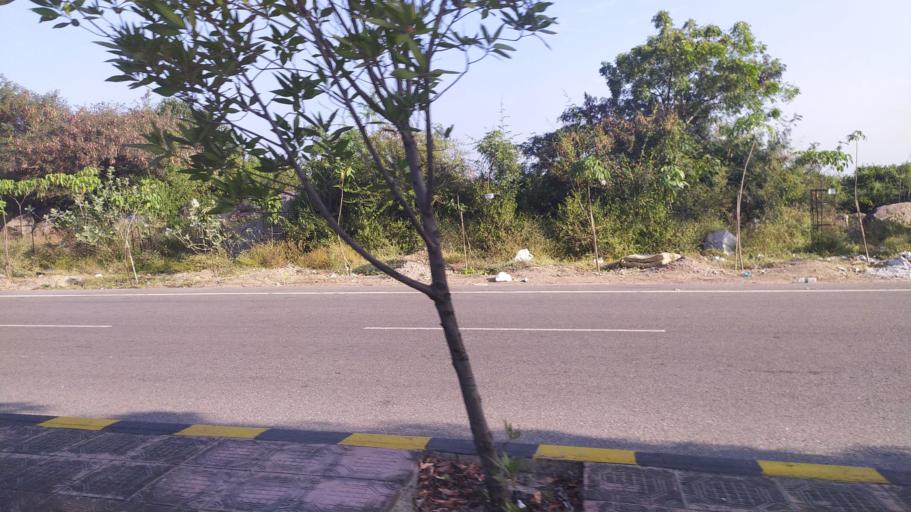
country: IN
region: Telangana
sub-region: Hyderabad
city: Hyderabad
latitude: 17.3218
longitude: 78.3847
